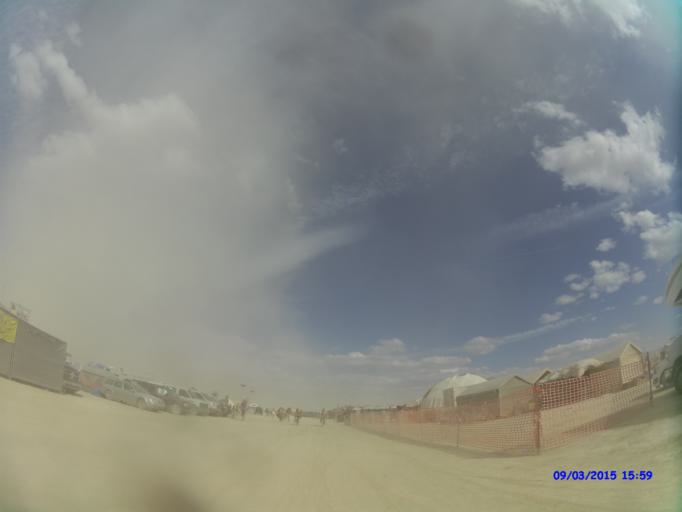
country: US
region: Nevada
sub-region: Pershing County
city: Lovelock
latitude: 40.7770
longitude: -119.2071
